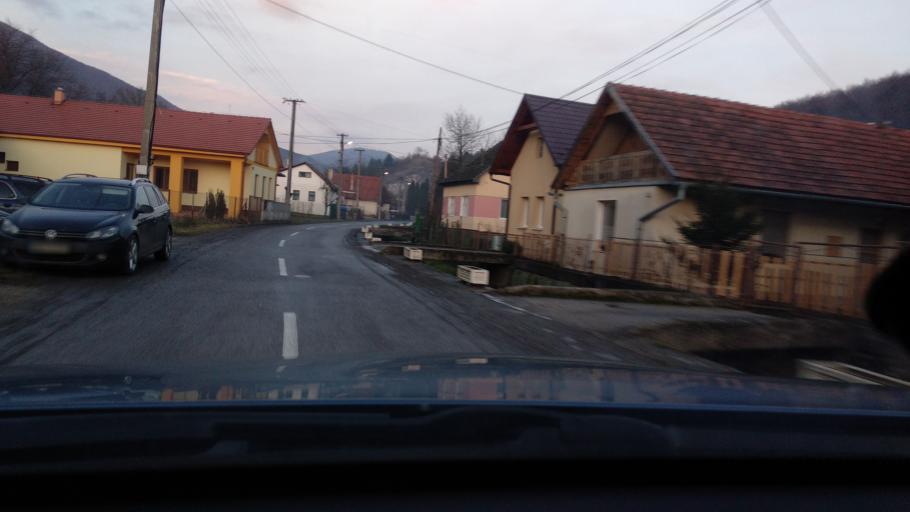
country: SK
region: Nitriansky
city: Banovce nad Bebravou
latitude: 48.8512
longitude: 18.2934
